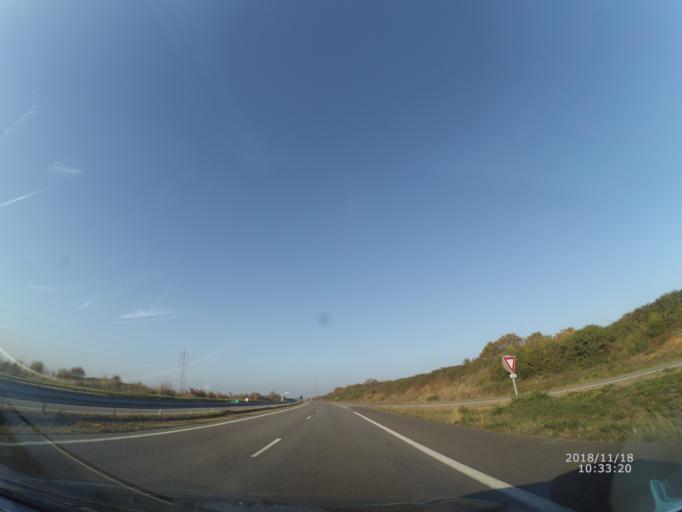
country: FR
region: Pays de la Loire
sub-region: Departement de la Loire-Atlantique
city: Saint-Jean-de-Boiseau
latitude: 47.1844
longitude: -1.7272
